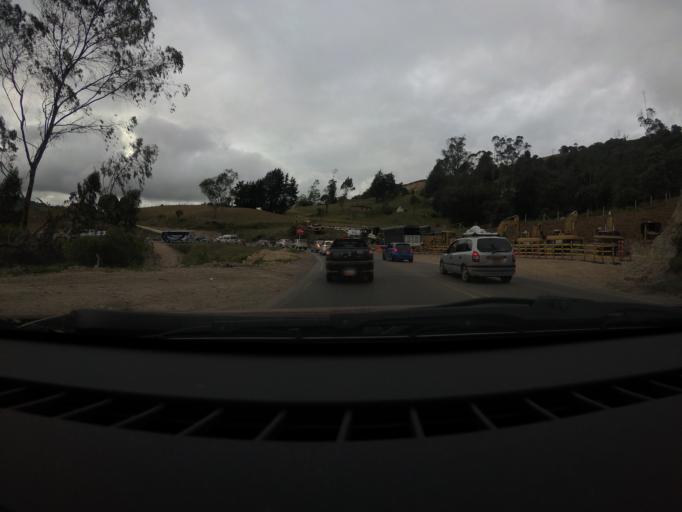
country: CO
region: Boyaca
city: Samaca
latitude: 5.4598
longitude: -73.4191
